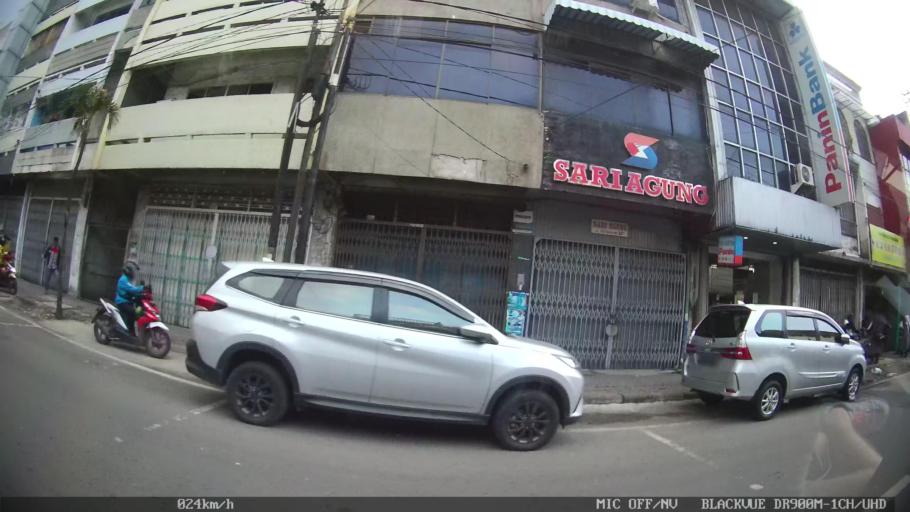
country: ID
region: North Sumatra
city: Medan
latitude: 3.5863
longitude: 98.6855
